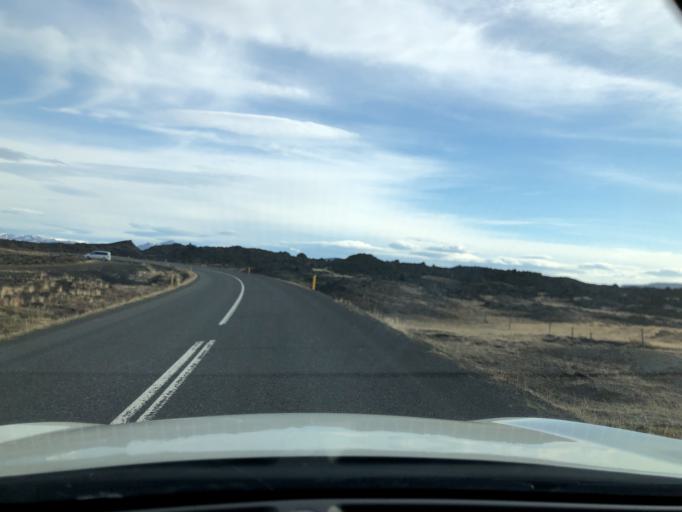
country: IS
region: Northeast
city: Laugar
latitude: 65.5626
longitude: -16.9431
